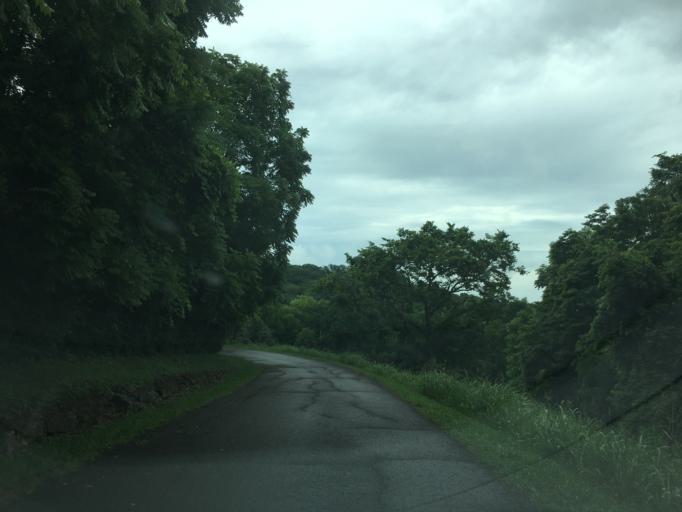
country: US
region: Tennessee
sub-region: Davidson County
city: Forest Hills
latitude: 36.0619
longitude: -86.8907
